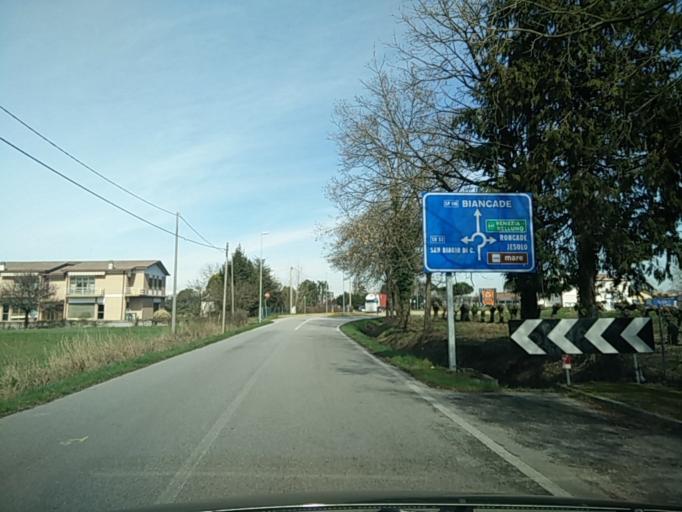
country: IT
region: Veneto
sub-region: Provincia di Treviso
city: Cendon
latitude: 45.6512
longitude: 12.3291
